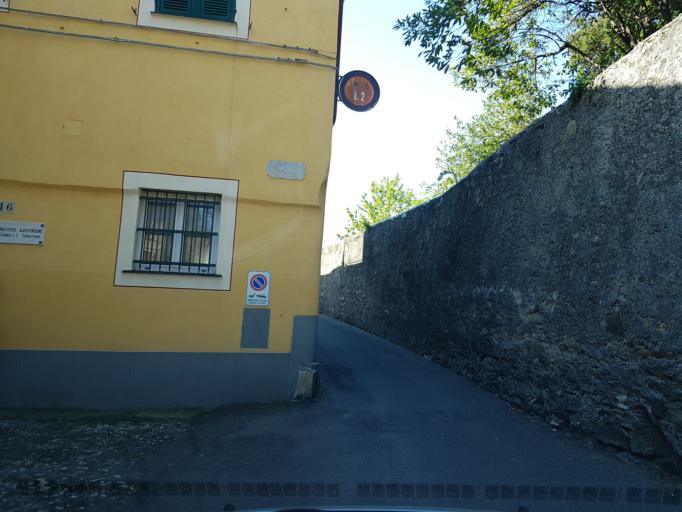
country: IT
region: Liguria
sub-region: Provincia di Genova
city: Genoa
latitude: 44.3923
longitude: 8.9778
